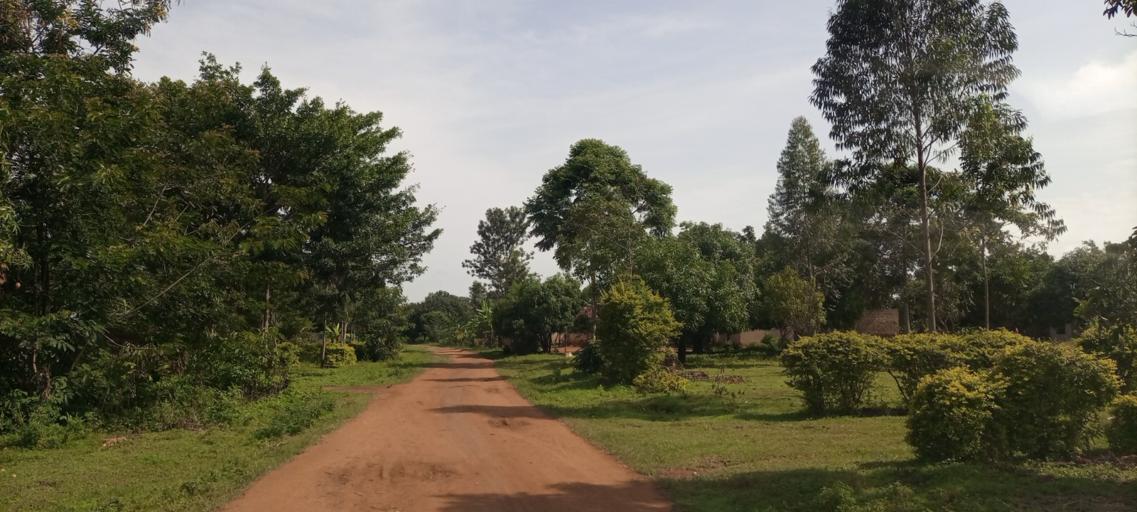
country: UG
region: Eastern Region
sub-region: Mbale District
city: Mbale
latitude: 1.1297
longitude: 34.0241
